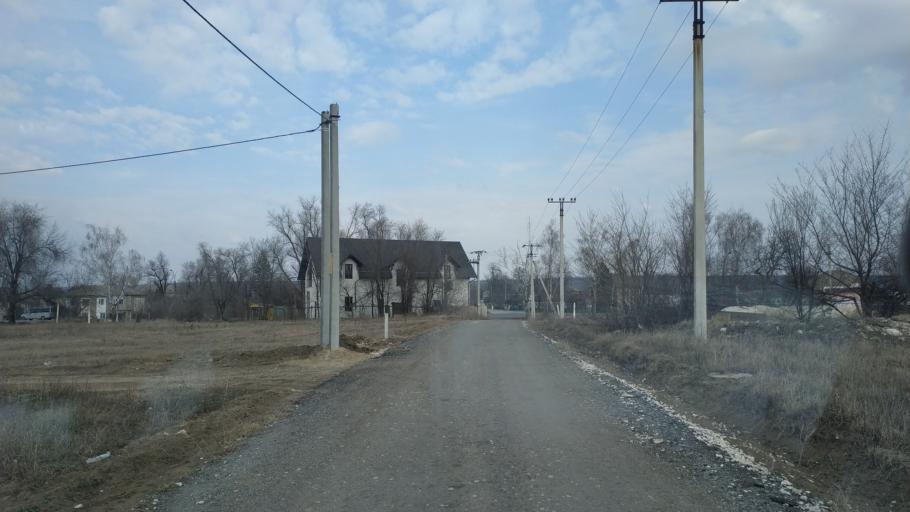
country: MD
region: Anenii Noi
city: Anenii Noi
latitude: 46.8986
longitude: 29.1334
